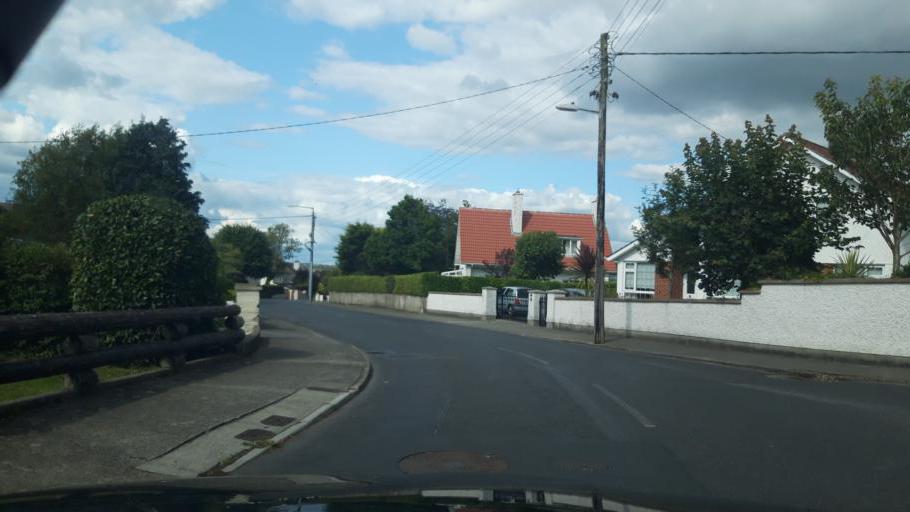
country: IE
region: Munster
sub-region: Waterford
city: Waterford
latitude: 52.2481
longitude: -7.1006
